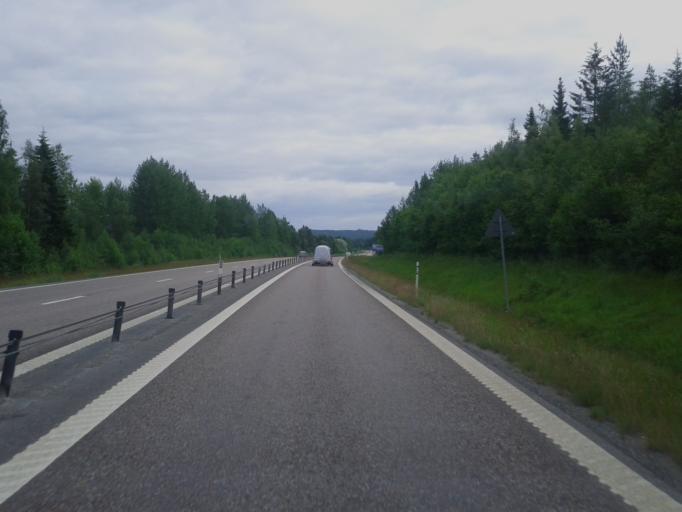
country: SE
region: Vaesternorrland
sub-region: OErnskoeldsviks Kommun
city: Kopmanholmen
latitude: 63.2870
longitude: 18.5887
